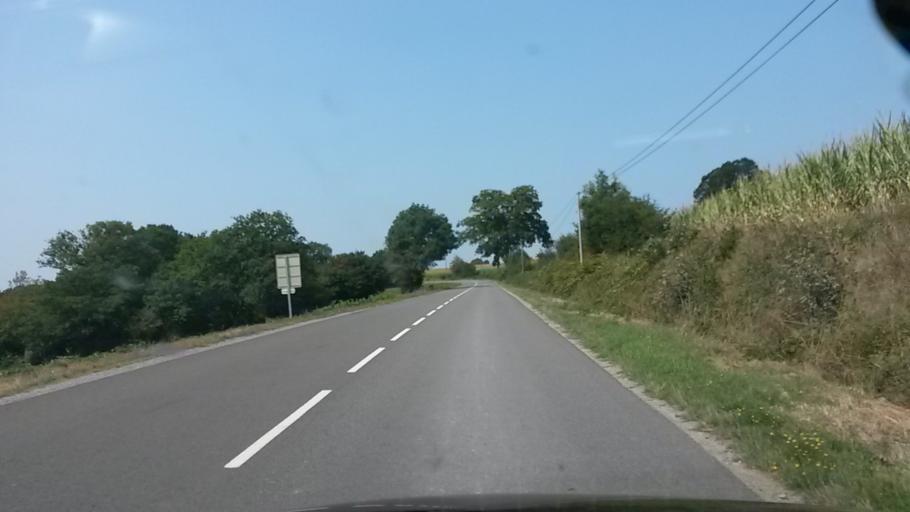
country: FR
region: Pays de la Loire
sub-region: Departement de la Mayenne
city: Villaines-la-Juhel
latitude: 48.3533
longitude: -0.2477
